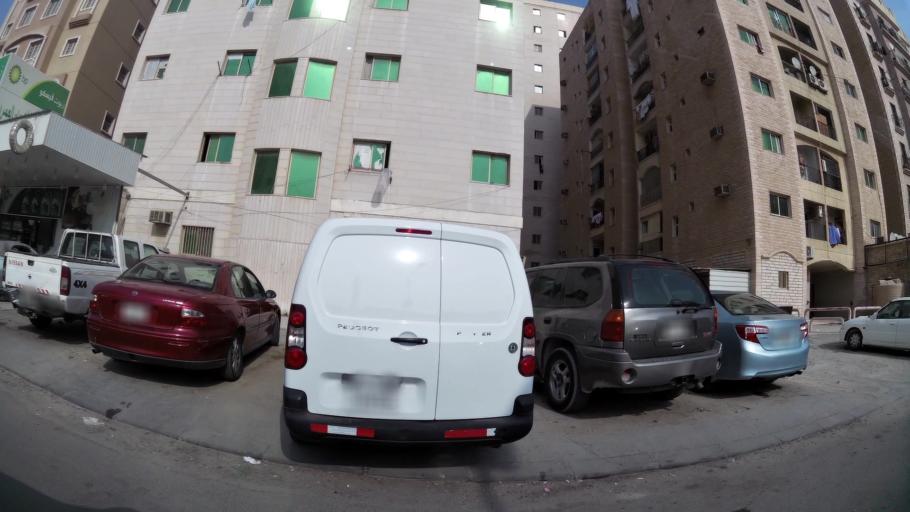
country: KW
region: Al Farwaniyah
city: Al Farwaniyah
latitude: 29.2749
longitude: 47.9559
